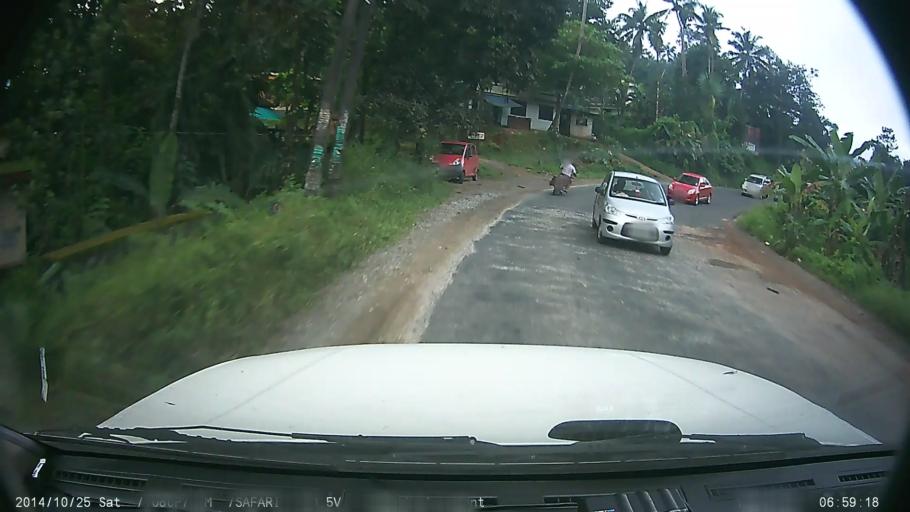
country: IN
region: Kerala
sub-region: Ernakulam
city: Piravam
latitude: 9.8868
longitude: 76.5921
